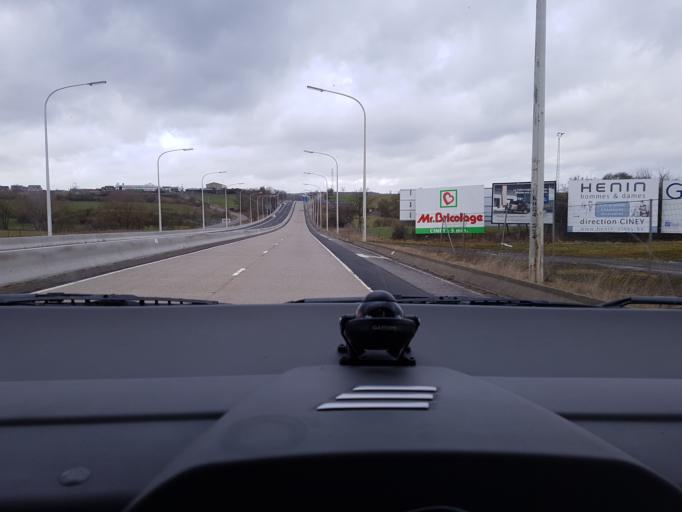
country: BE
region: Wallonia
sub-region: Province de Namur
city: Rochefort
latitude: 50.2703
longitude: 5.2428
